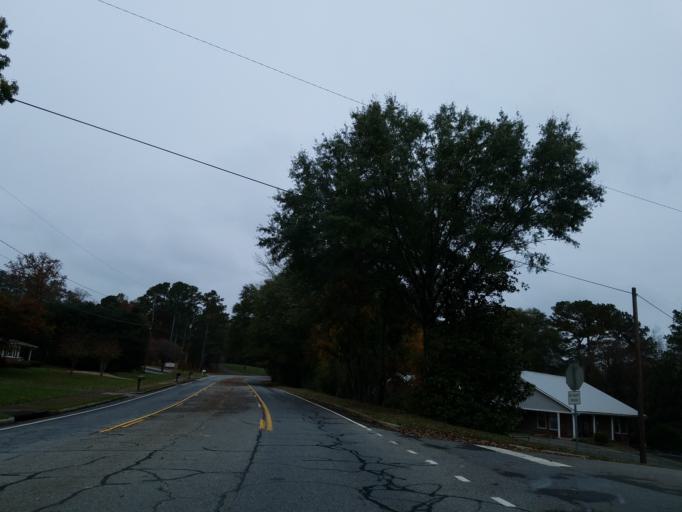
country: US
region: Georgia
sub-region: Cherokee County
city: Canton
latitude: 34.3124
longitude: -84.5543
